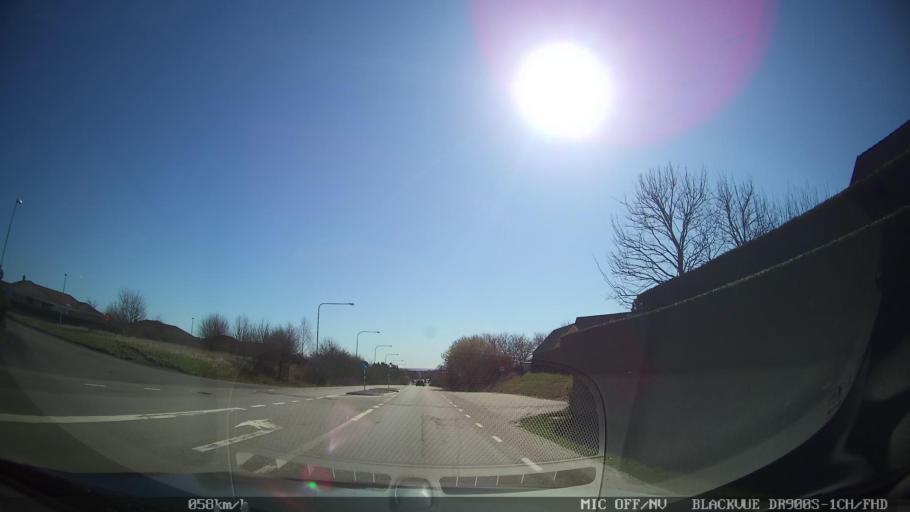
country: SE
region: Skane
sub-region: Ystads Kommun
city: Ystad
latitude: 55.4364
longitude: 13.7959
